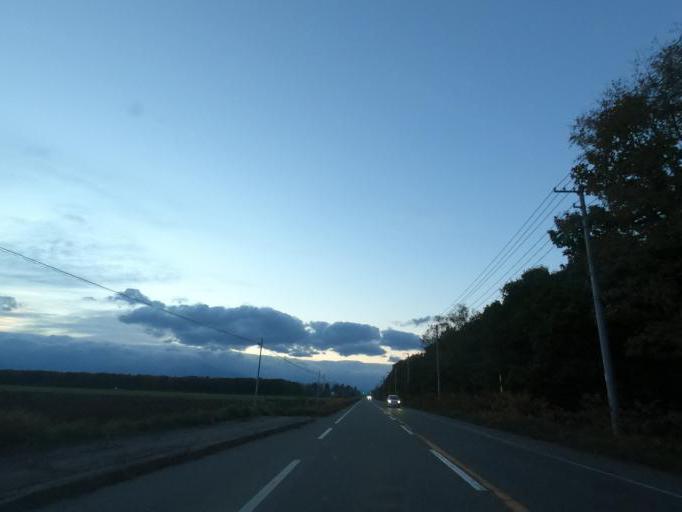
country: JP
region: Hokkaido
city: Obihiro
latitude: 42.6768
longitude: 143.1622
